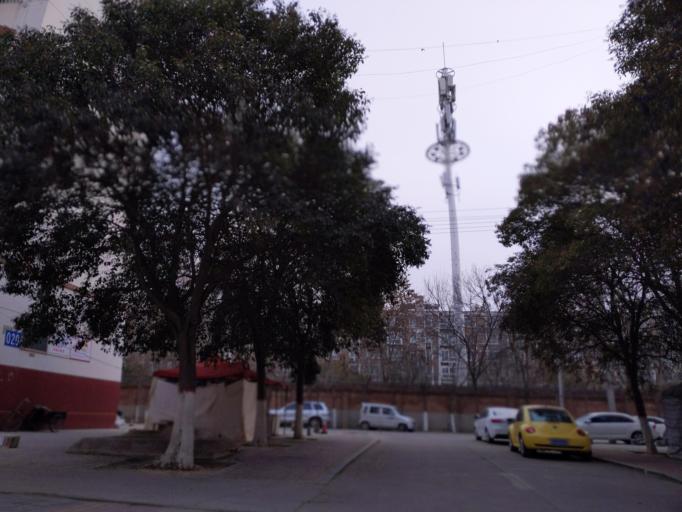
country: CN
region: Henan Sheng
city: Zhongyuanlu
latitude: 35.7559
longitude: 115.0512
